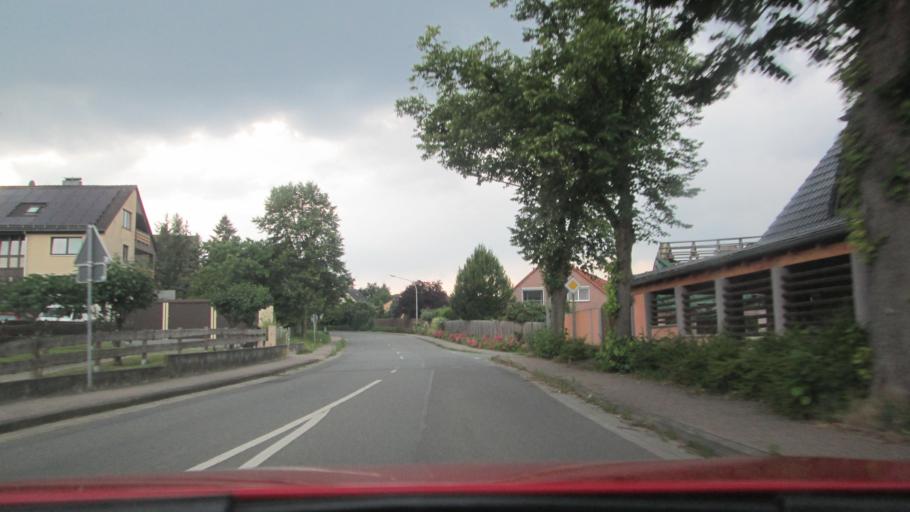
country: DE
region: Lower Saxony
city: Lehre
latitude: 52.3507
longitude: 10.7087
